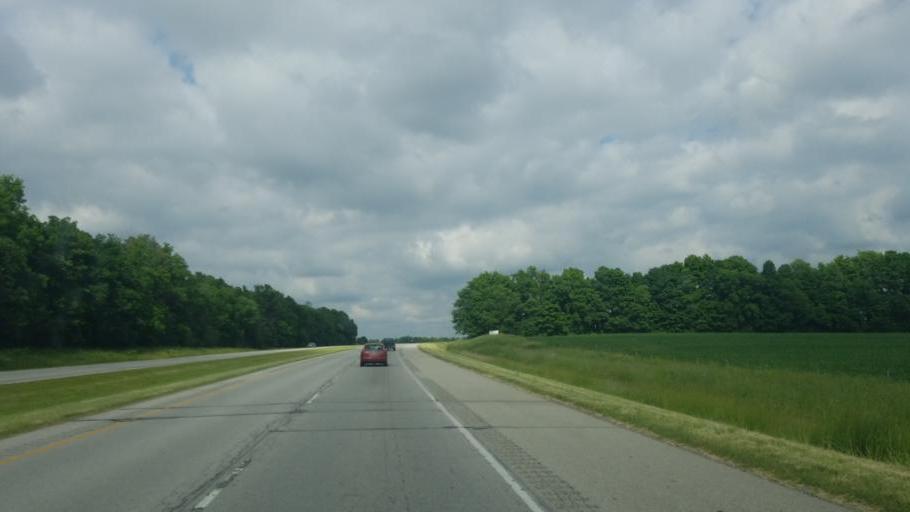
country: US
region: Indiana
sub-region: Kosciusko County
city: Warsaw
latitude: 41.2679
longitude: -85.9524
